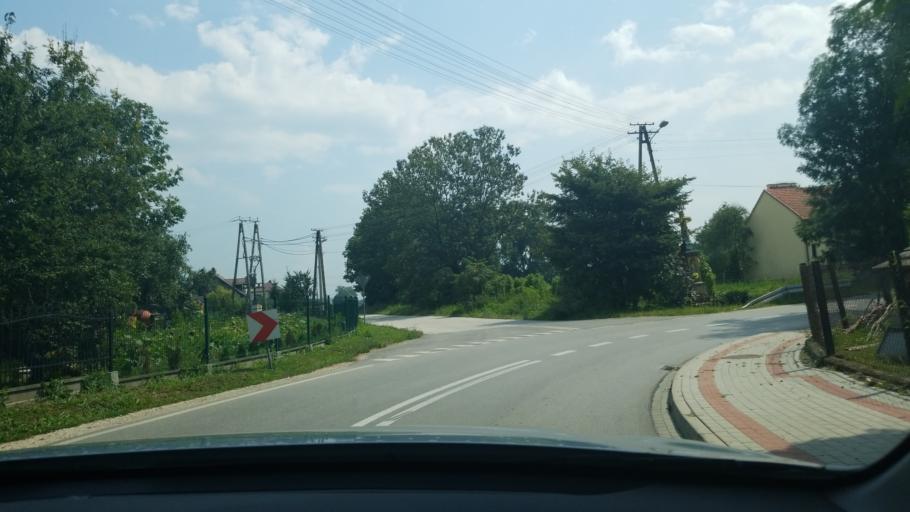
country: PL
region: Lesser Poland Voivodeship
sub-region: Powiat bochenski
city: Dziewin
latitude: 50.1166
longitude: 20.5169
